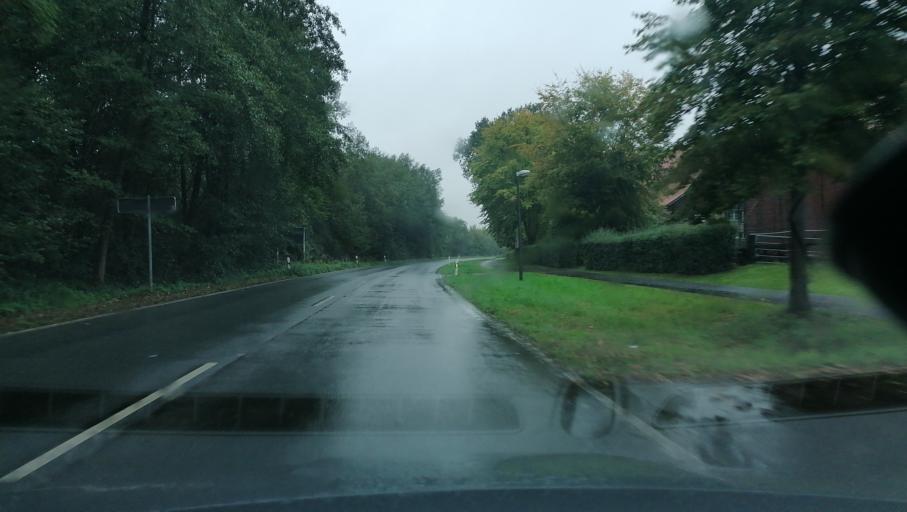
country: DE
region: North Rhine-Westphalia
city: Oer-Erkenschwick
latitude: 51.5909
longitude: 7.2568
